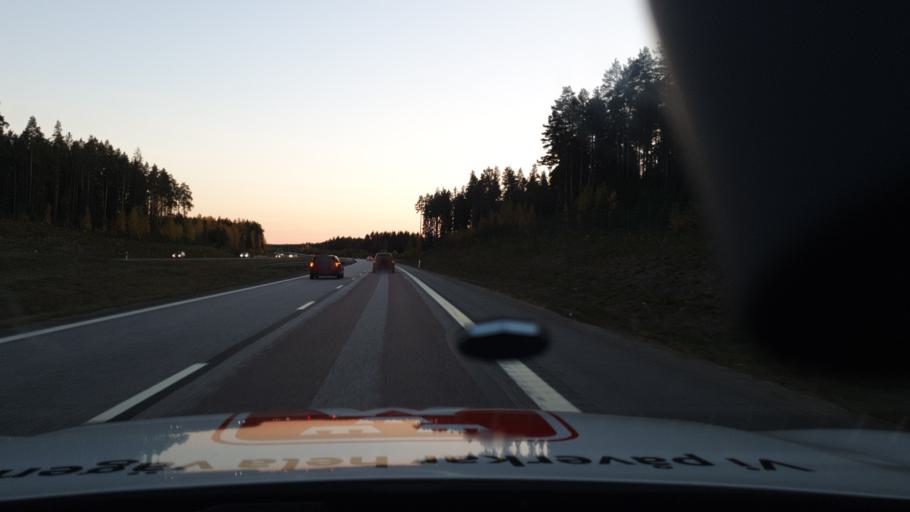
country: SE
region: Uppsala
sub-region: Tierps Kommun
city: Tierp
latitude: 60.2820
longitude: 17.5029
